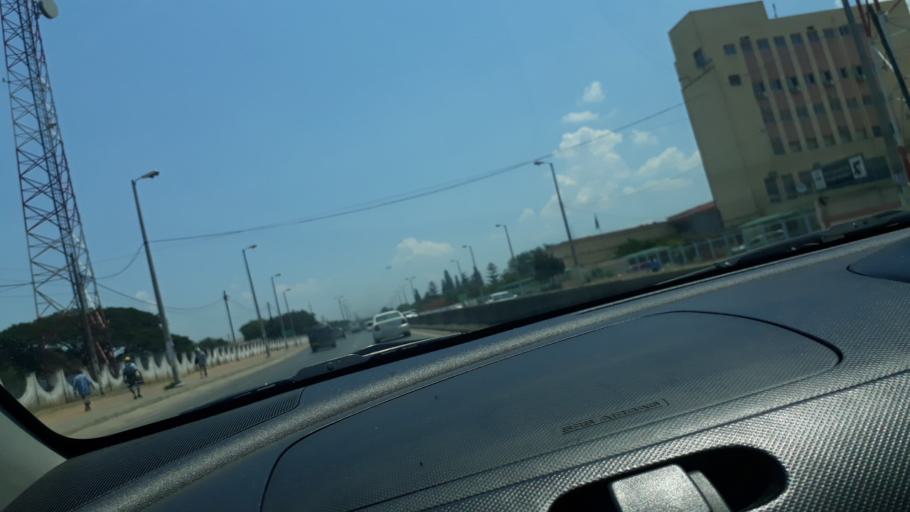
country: MZ
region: Maputo City
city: Maputo
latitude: -25.9360
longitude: 32.5491
